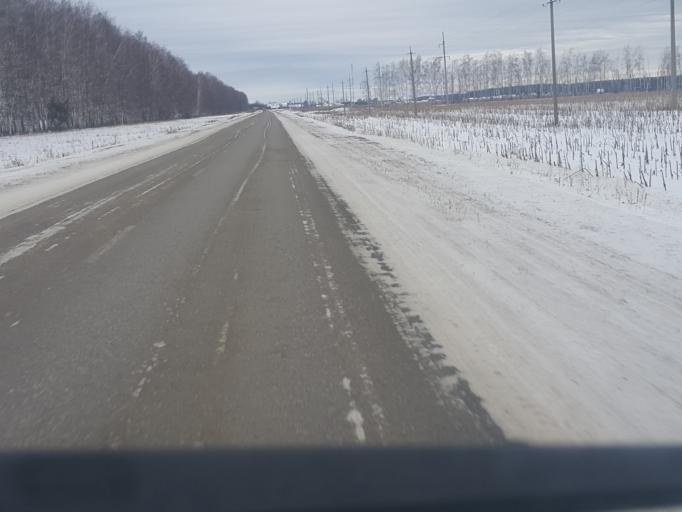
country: RU
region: Tambov
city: Rasskazovo
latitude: 52.8151
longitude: 41.7942
